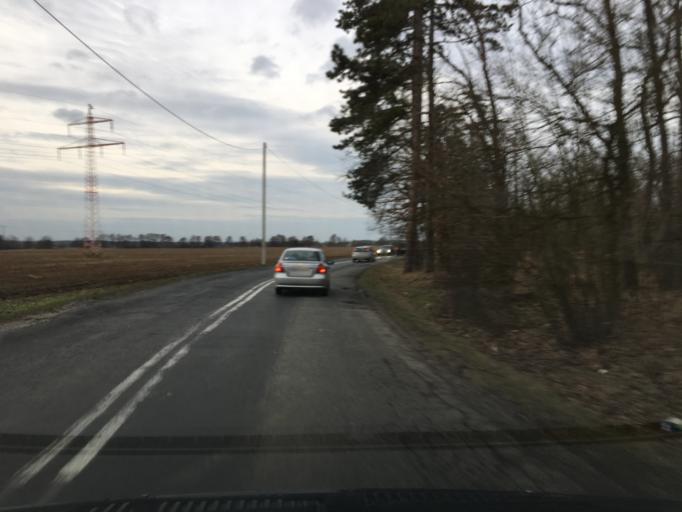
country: PL
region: Opole Voivodeship
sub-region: Powiat krapkowicki
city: Januszkowice
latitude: 50.3766
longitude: 18.1422
